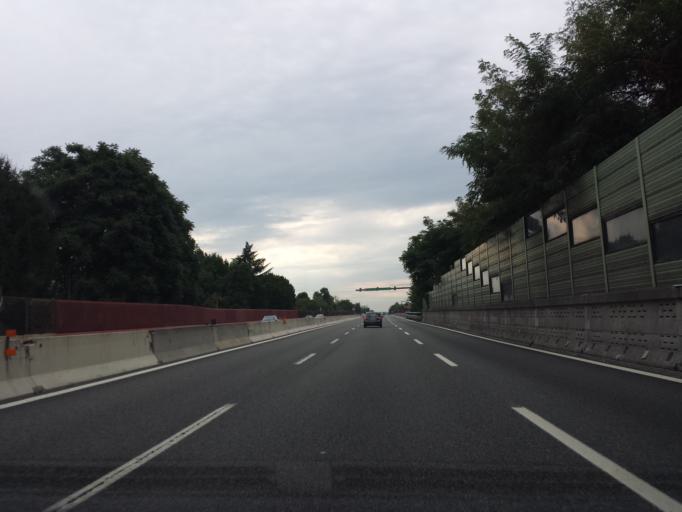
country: IT
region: Lombardy
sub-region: Provincia di Varese
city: Cassano Magnago
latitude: 45.6608
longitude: 8.8074
